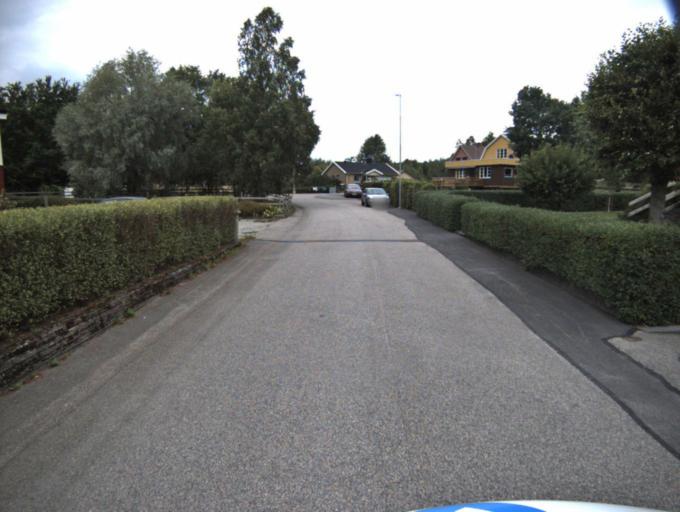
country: SE
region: Vaestra Goetaland
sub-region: Boras Kommun
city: Dalsjofors
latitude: 57.8290
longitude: 13.1956
